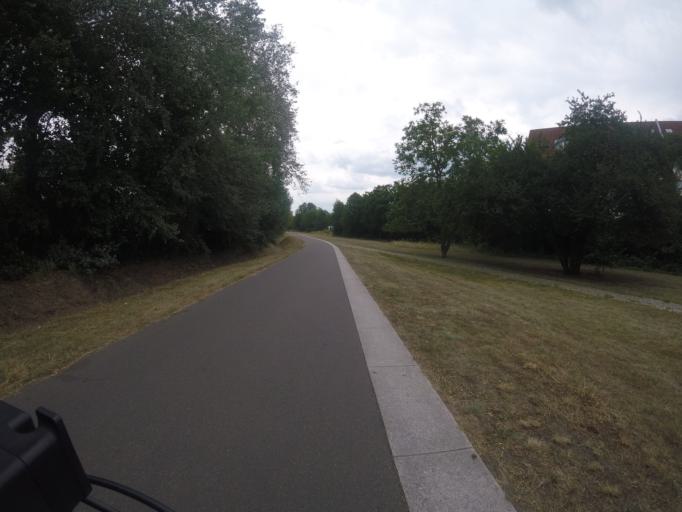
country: DE
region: Berlin
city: Wilhelmstadt
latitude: 52.5304
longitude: 13.1805
